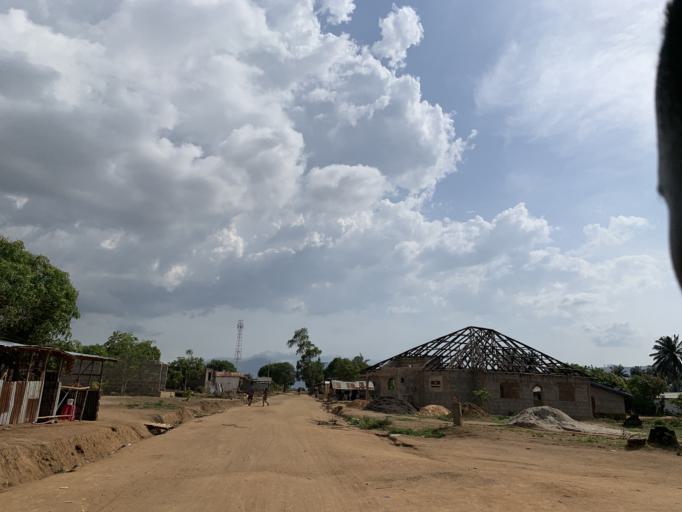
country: SL
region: Western Area
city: Waterloo
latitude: 8.3480
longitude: -13.0383
